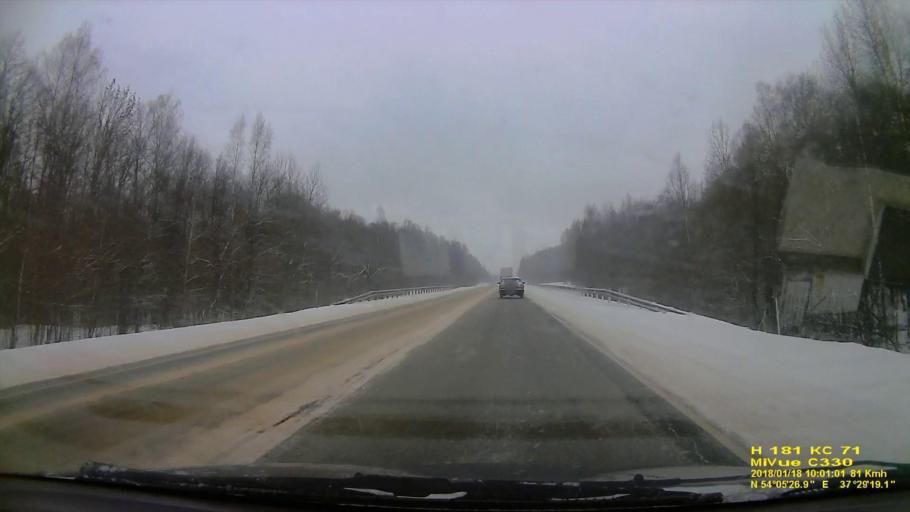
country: RU
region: Tula
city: Pervomayskiy
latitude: 54.0909
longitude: 37.4886
